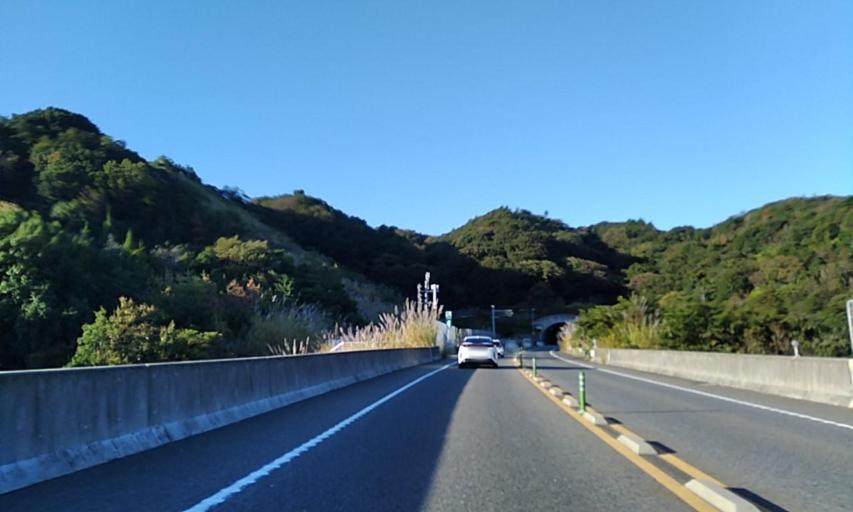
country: JP
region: Wakayama
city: Wakayama-shi
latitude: 34.3245
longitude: 135.2035
